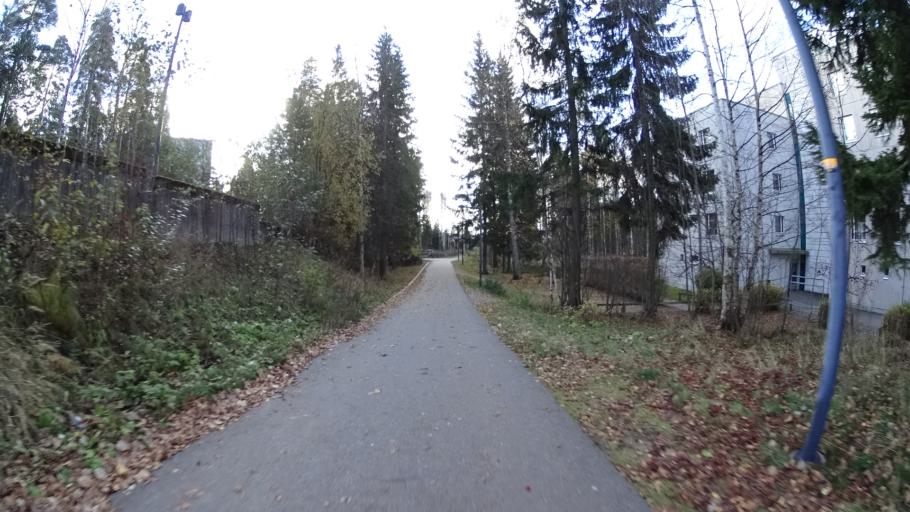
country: FI
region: Uusimaa
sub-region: Helsinki
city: Teekkarikylae
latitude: 60.2566
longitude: 24.8499
